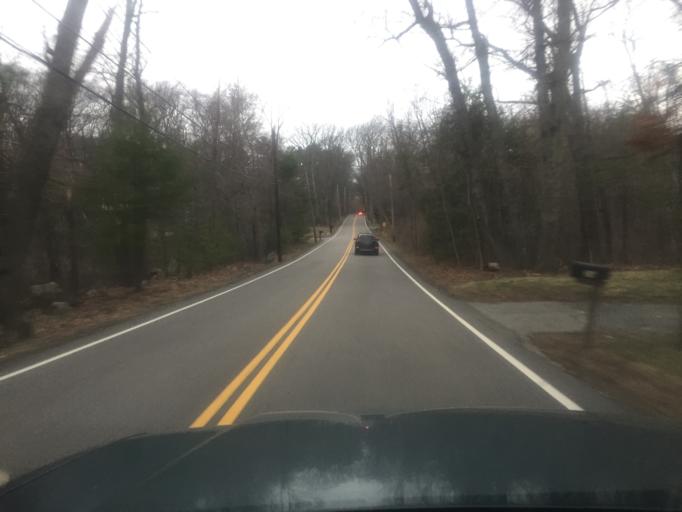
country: US
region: Massachusetts
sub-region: Norfolk County
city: Medway
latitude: 42.1472
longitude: -71.4378
